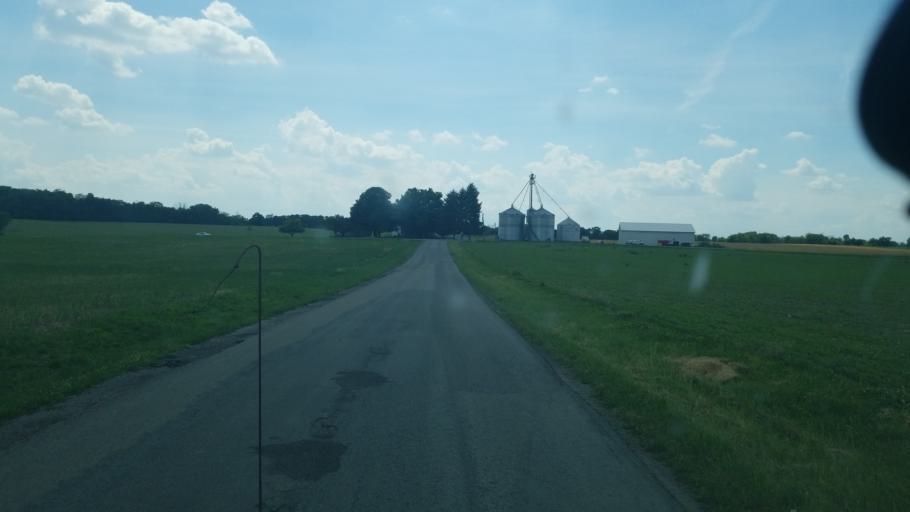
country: US
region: Ohio
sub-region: Highland County
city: Leesburg
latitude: 39.2933
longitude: -83.5773
